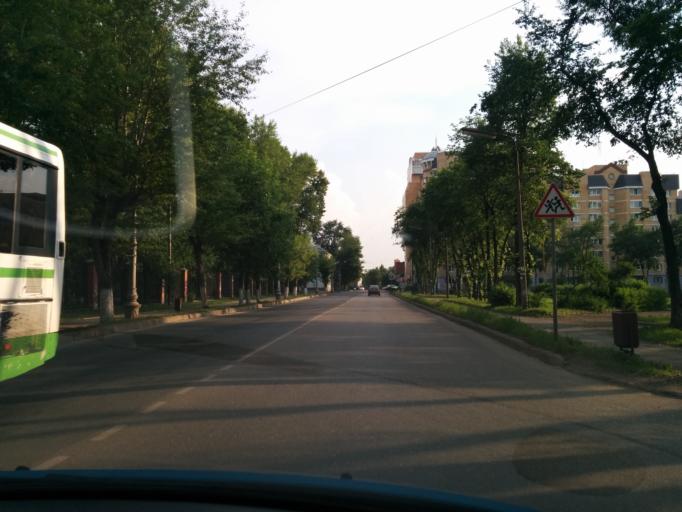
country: RU
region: Perm
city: Perm
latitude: 58.0234
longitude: 56.2921
